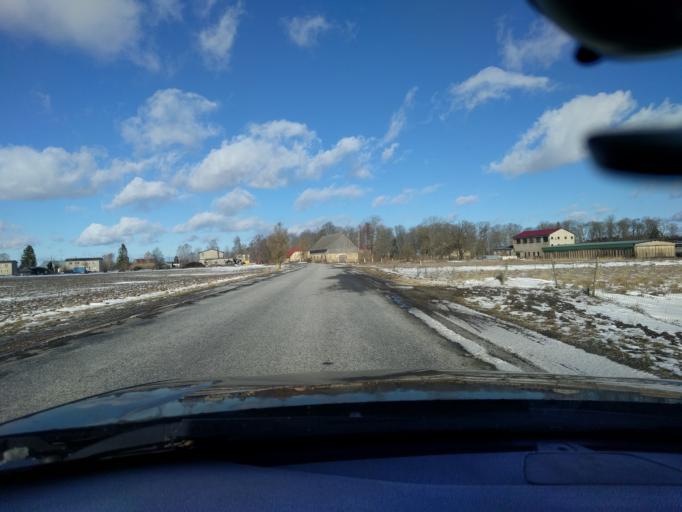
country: EE
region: Harju
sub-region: Raasiku vald
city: Raasiku
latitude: 59.3333
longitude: 25.1562
